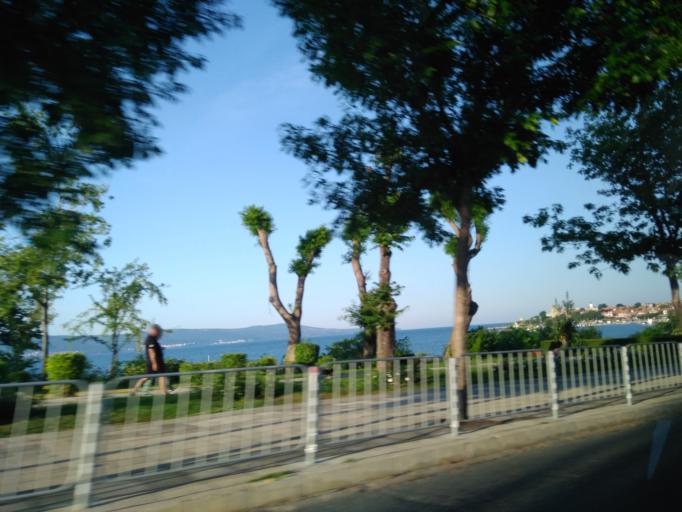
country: BG
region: Burgas
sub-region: Obshtina Nesebur
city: Nesebar
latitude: 42.6604
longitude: 27.7239
